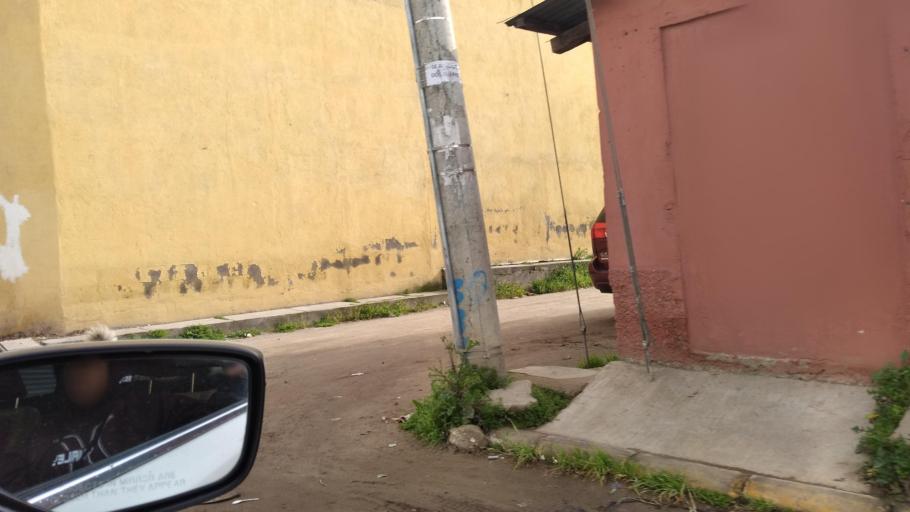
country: GT
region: Quetzaltenango
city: Quetzaltenango
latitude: 14.8583
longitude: -91.5194
